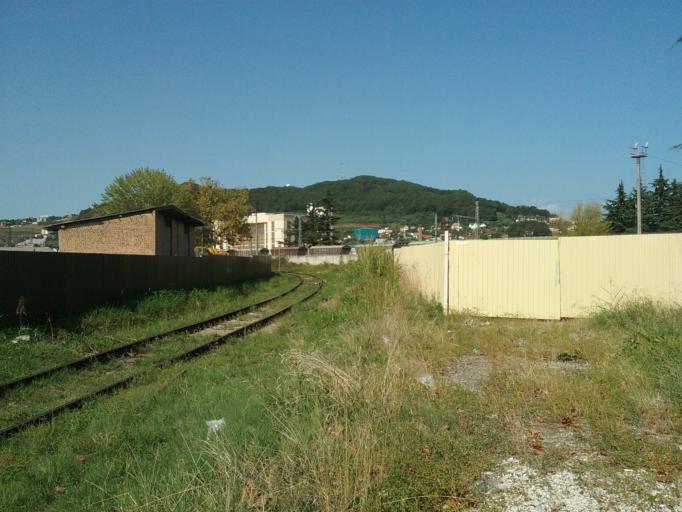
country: RU
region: Krasnodarskiy
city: Vysokoye
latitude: 43.3999
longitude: 39.9937
